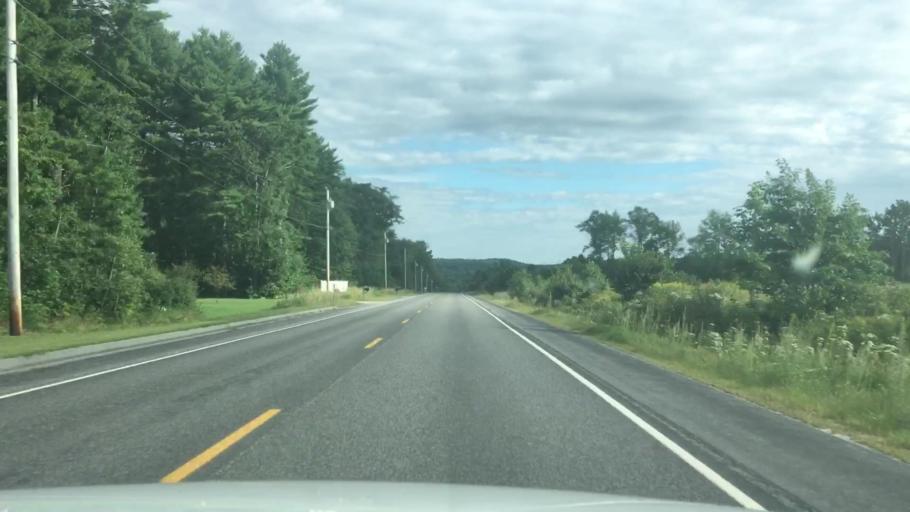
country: US
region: Maine
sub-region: Androscoggin County
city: Lisbon
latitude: 44.0620
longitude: -70.0852
